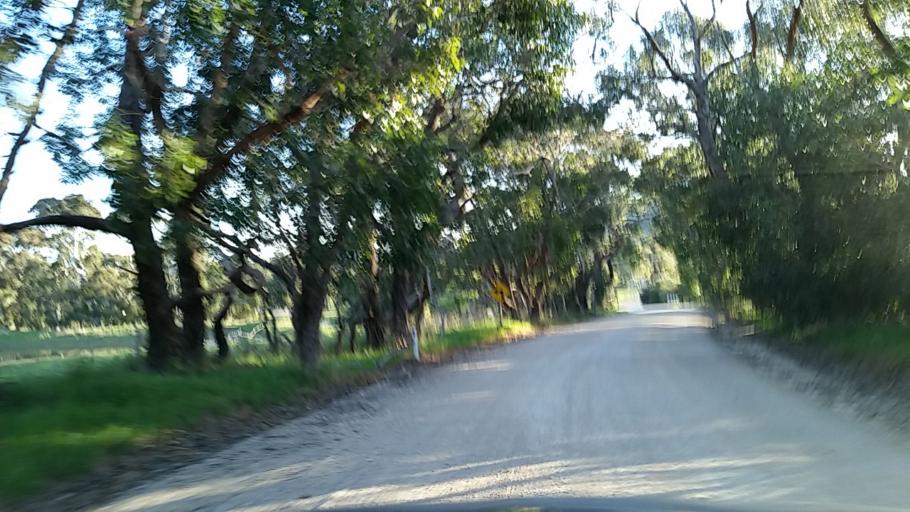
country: AU
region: South Australia
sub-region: Alexandrina
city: Mount Compass
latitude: -35.3140
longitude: 138.6702
